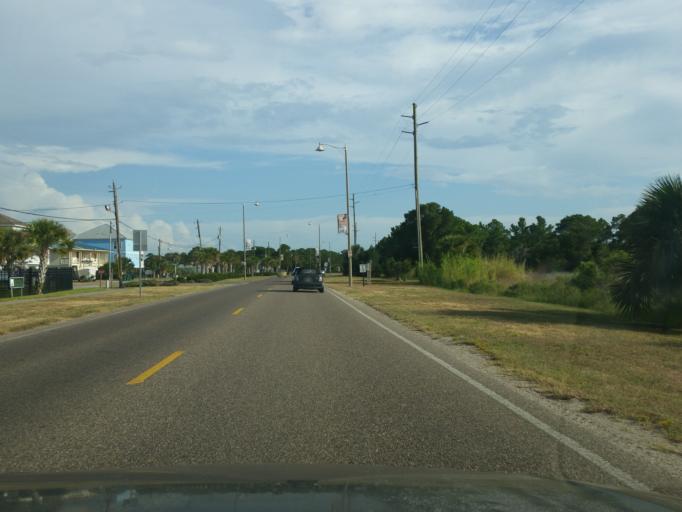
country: US
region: Alabama
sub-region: Mobile County
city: Dauphin Island
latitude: 30.2617
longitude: -88.1139
